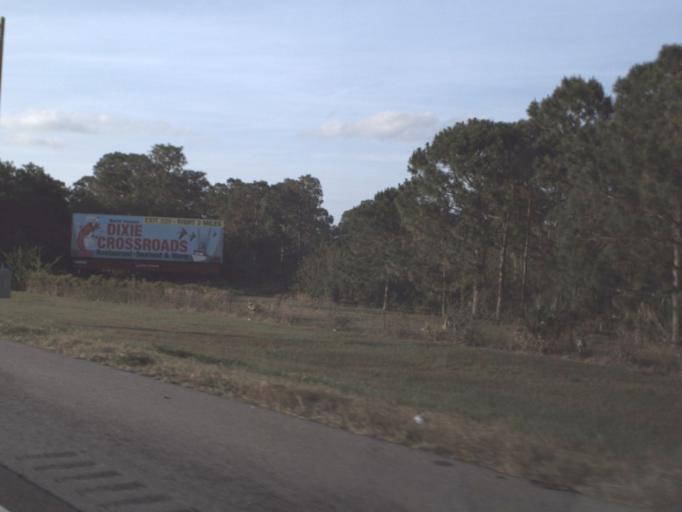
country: US
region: Florida
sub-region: Brevard County
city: Port Saint John
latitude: 28.4812
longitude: -80.8222
